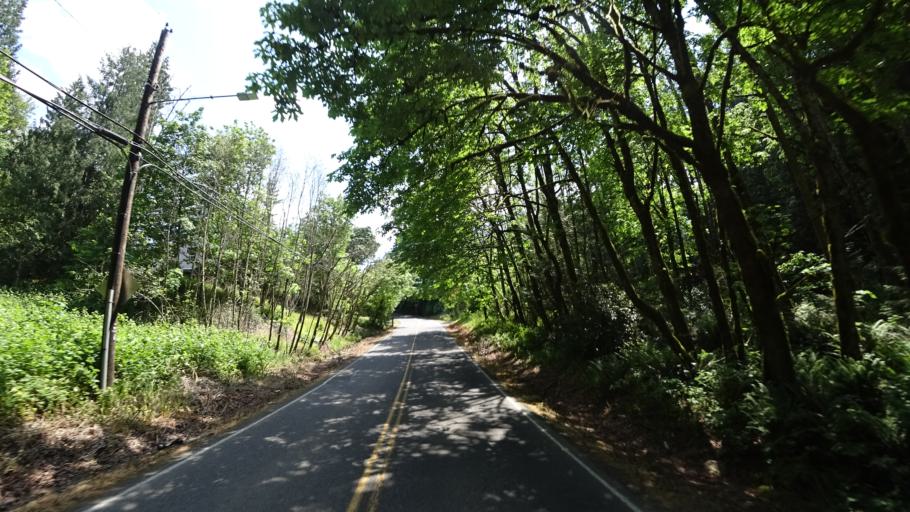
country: US
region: Oregon
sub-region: Clackamas County
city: Happy Valley
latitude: 45.4688
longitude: -122.5097
